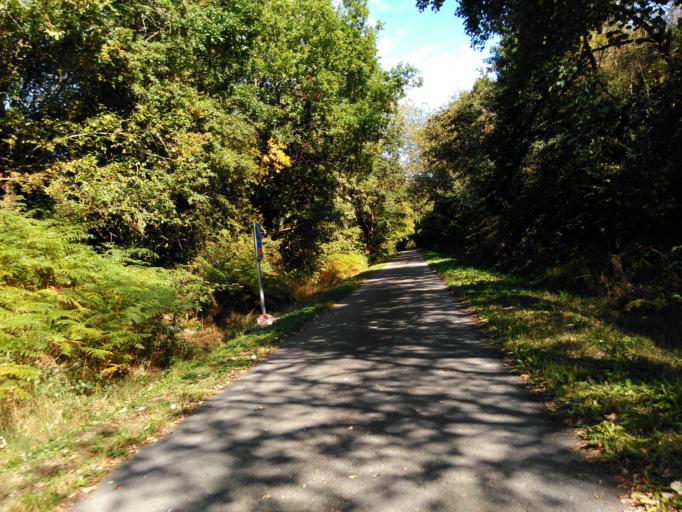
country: BE
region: Wallonia
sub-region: Province du Luxembourg
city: Bastogne
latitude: 50.0199
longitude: 5.7425
